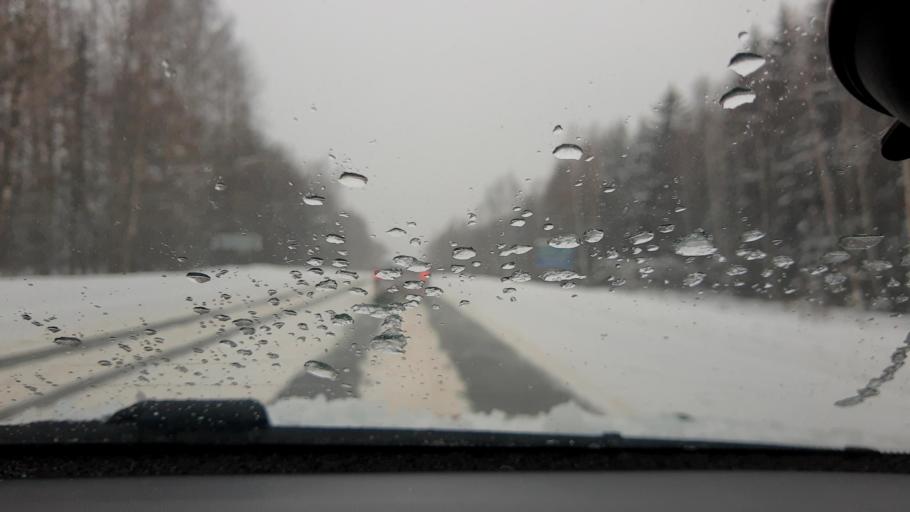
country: RU
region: Nizjnij Novgorod
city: Pervomayskiy
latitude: 56.6280
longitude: 43.2259
